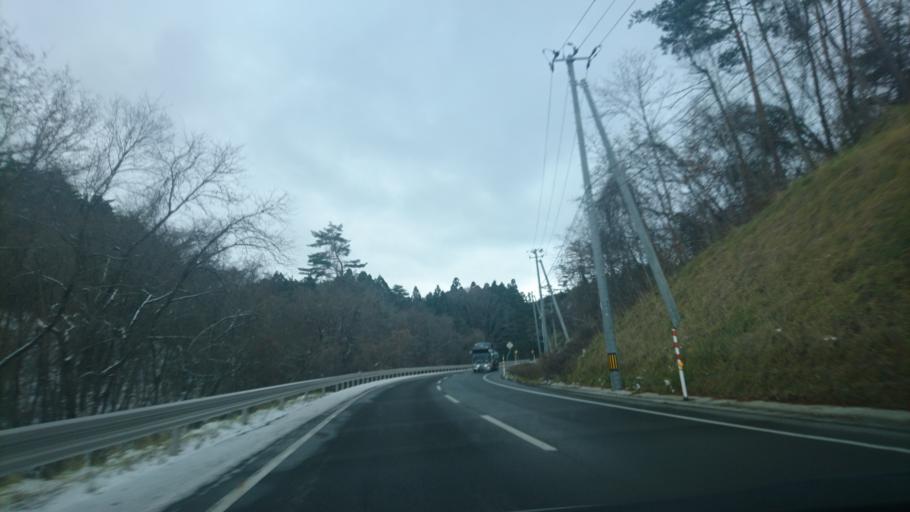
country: JP
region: Iwate
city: Mizusawa
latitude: 39.1613
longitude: 141.2481
